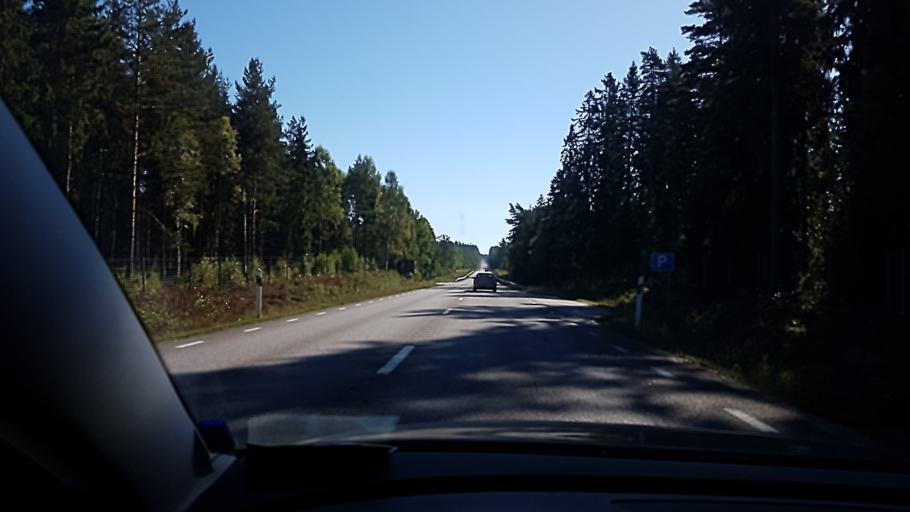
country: SE
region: Kronoberg
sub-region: Lessebo Kommun
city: Hovmantorp
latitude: 56.7927
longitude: 15.1269
